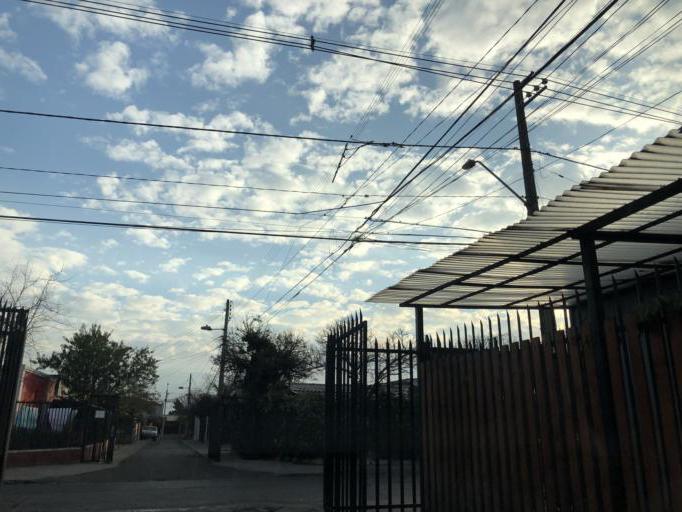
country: CL
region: Santiago Metropolitan
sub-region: Provincia de Cordillera
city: Puente Alto
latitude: -33.6151
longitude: -70.5808
